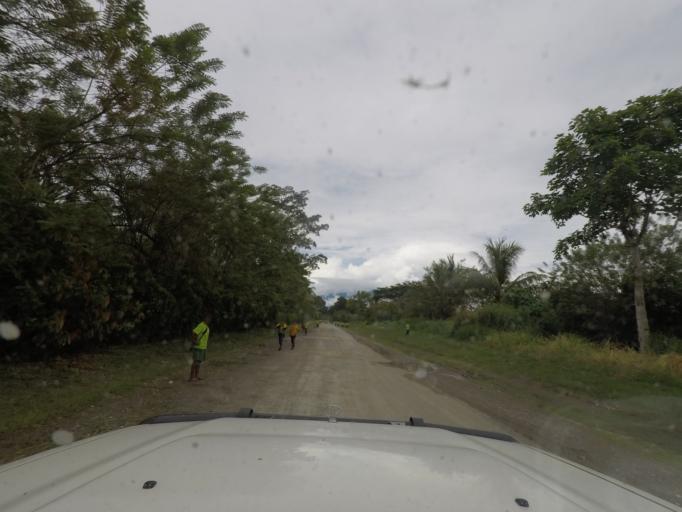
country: PG
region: Eastern Highlands
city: Goroka
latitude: -5.6677
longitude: 145.4993
